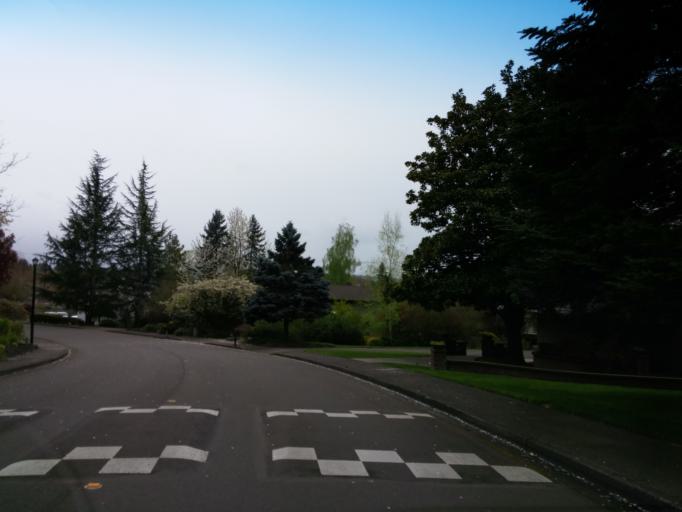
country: US
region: Oregon
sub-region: Washington County
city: Oak Hills
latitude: 45.5234
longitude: -122.8533
